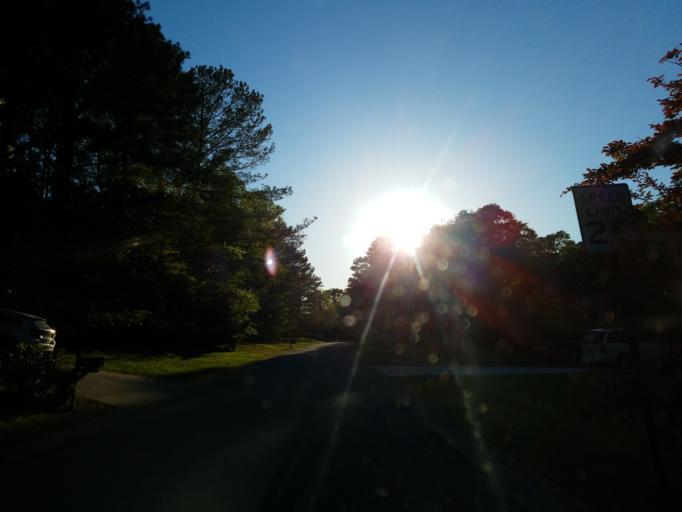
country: US
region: Georgia
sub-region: Cobb County
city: Powder Springs
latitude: 33.9199
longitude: -84.6323
